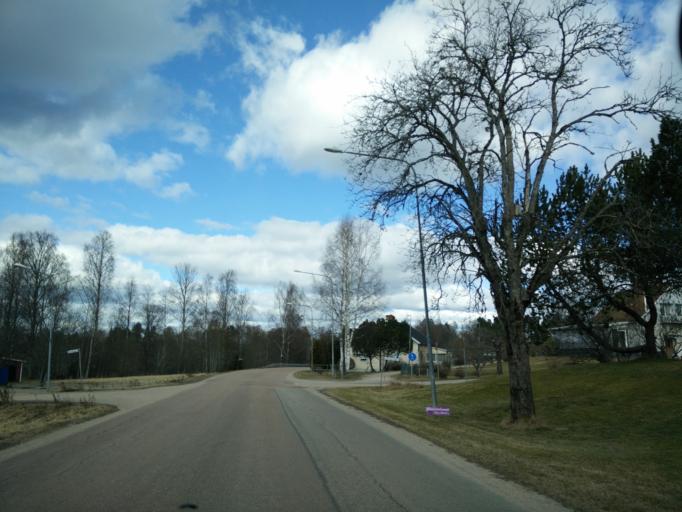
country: SE
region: Vaermland
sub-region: Hagfors Kommun
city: Hagfors
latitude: 59.9988
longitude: 13.5947
